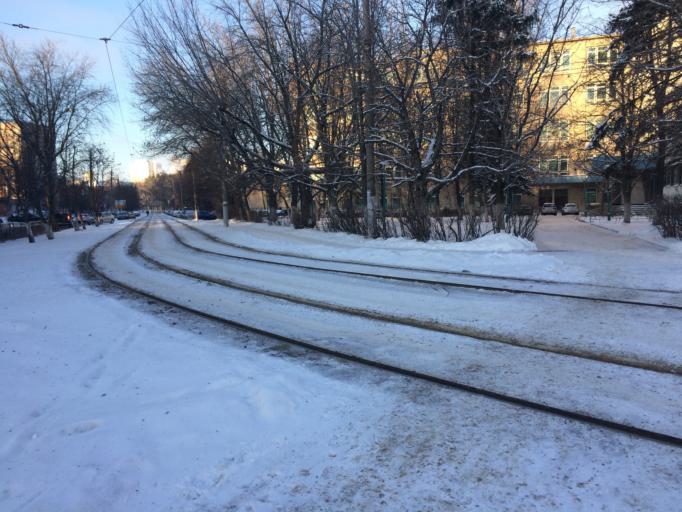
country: RU
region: Tula
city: Tula
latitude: 54.1746
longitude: 37.5932
